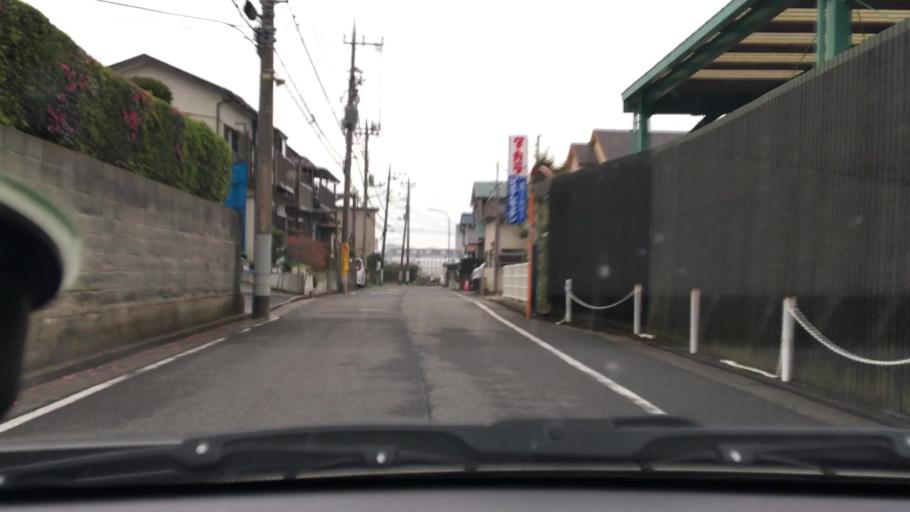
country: JP
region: Kanagawa
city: Yokohama
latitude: 35.5182
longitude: 139.6052
